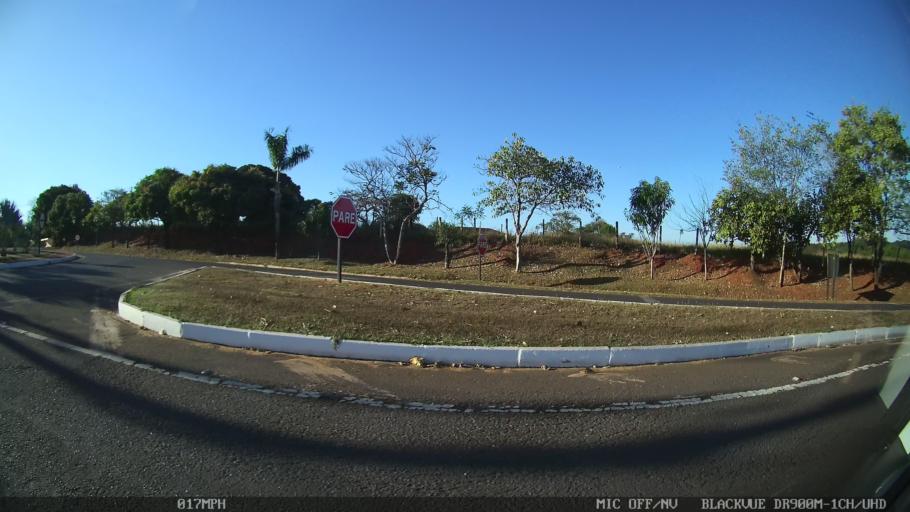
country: BR
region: Sao Paulo
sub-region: Guapiacu
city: Guapiacu
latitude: -20.7905
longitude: -49.2218
